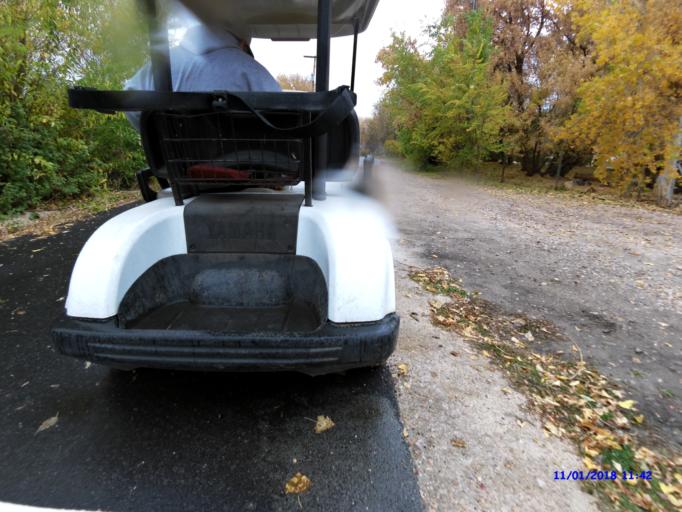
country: US
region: Utah
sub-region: Weber County
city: Ogden
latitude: 41.2333
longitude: -111.9848
